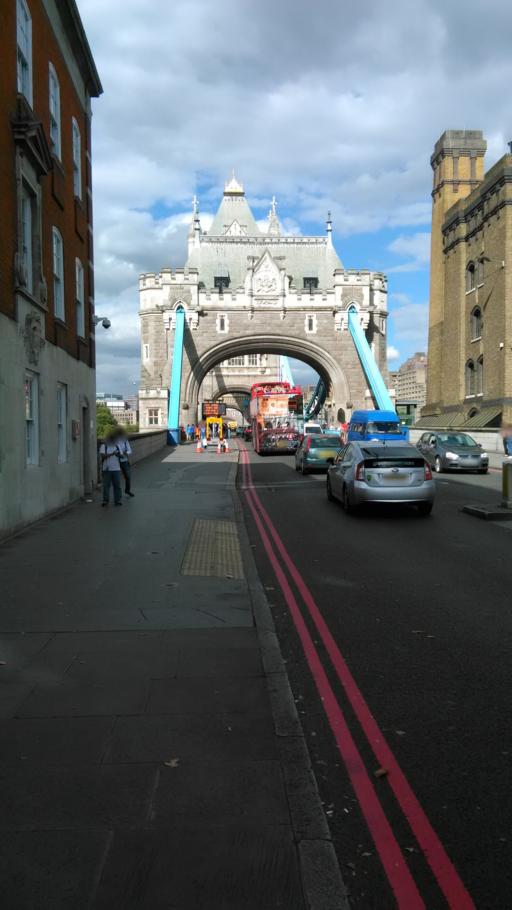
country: GB
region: England
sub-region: Greater London
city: City of London
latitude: 51.5039
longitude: -0.0765
